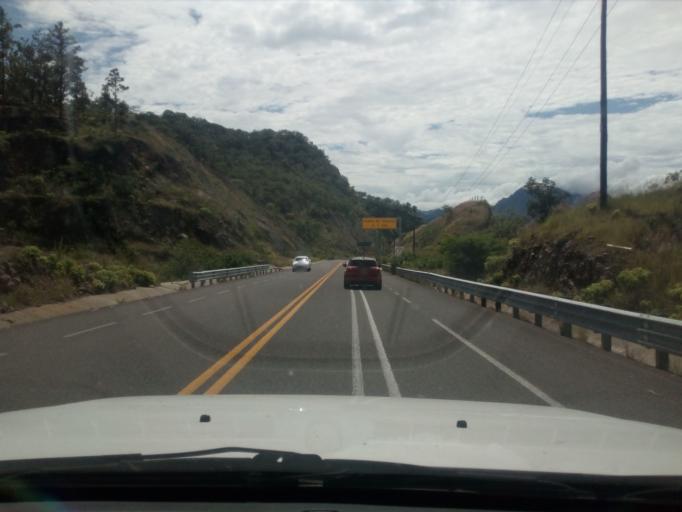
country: MX
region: Durango
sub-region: Pueblo Nuevo
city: La Ciudad
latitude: 23.5586
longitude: -105.7531
